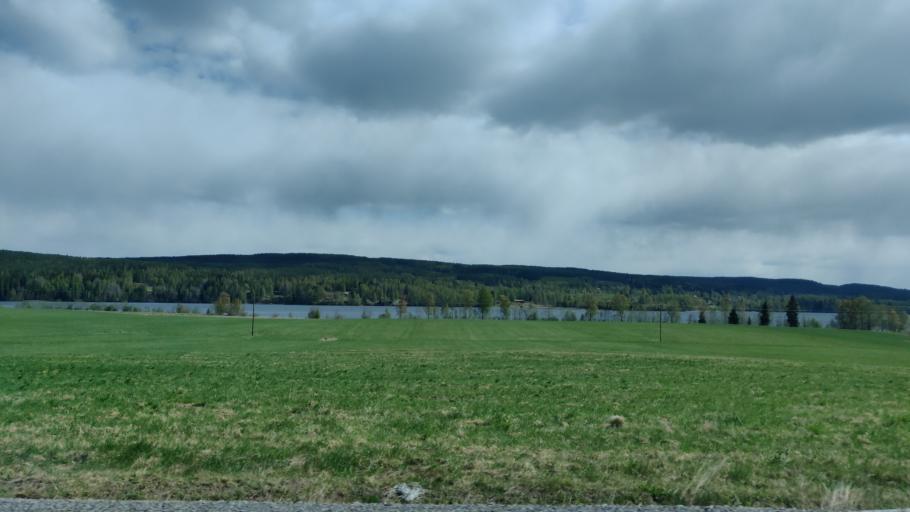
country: SE
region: Vaermland
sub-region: Munkfors Kommun
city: Munkfors
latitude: 59.8623
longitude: 13.7070
